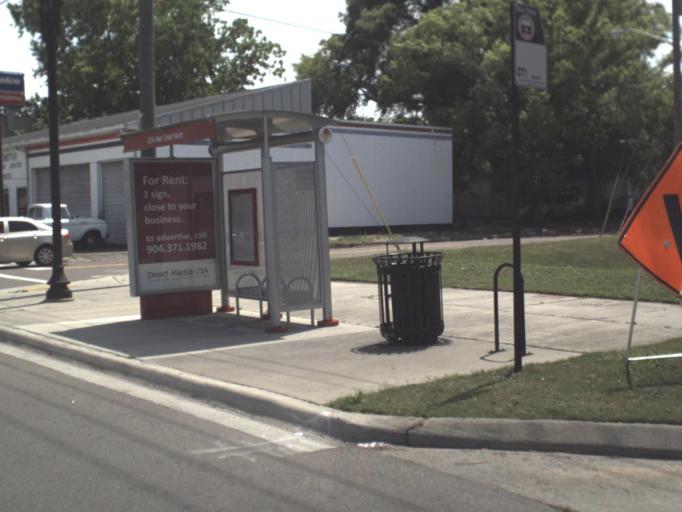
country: US
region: Florida
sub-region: Duval County
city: Jacksonville
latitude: 30.3580
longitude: -81.6539
